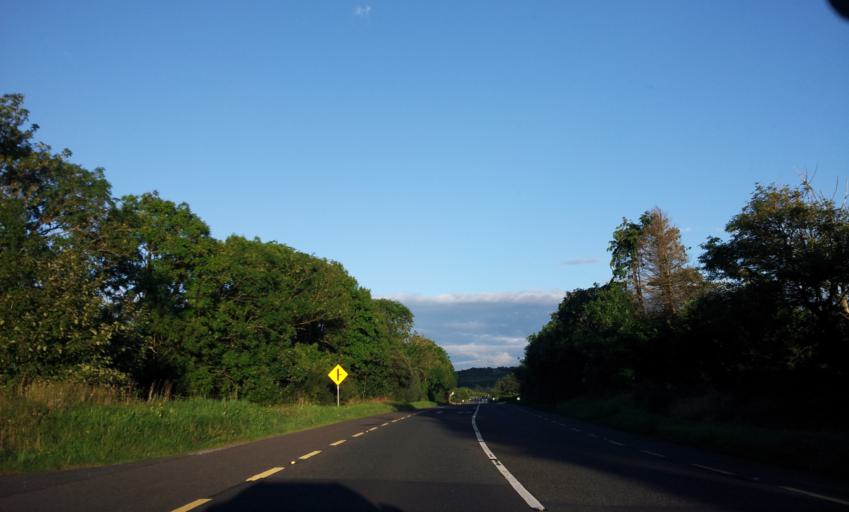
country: IE
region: Munster
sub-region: County Limerick
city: Abbeyfeale
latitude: 52.3876
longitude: -9.2401
